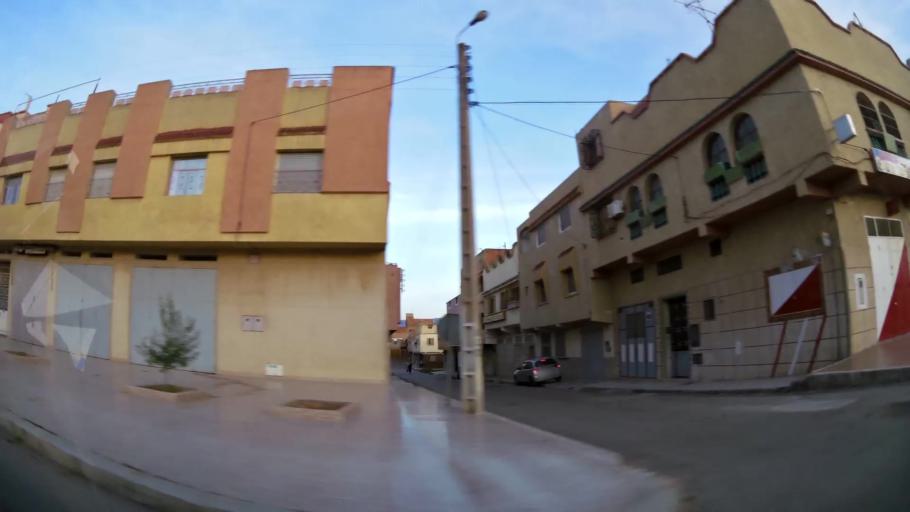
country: MA
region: Oriental
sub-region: Oujda-Angad
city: Oujda
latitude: 34.6796
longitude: -1.8781
